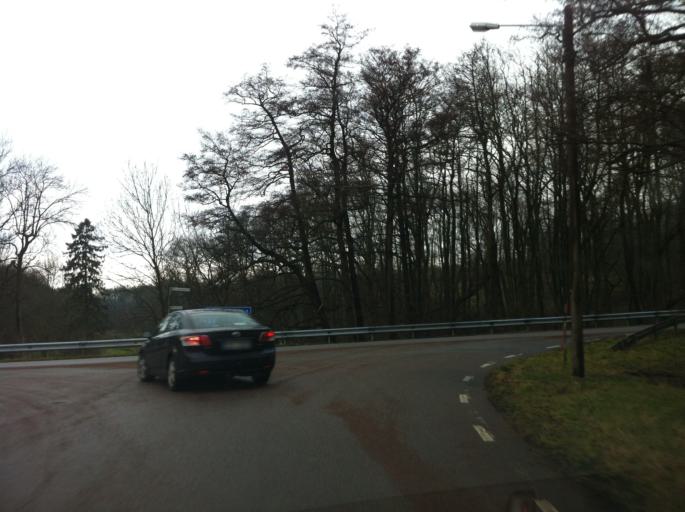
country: SE
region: Skane
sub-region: Helsingborg
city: Barslov
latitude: 55.9903
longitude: 12.8225
